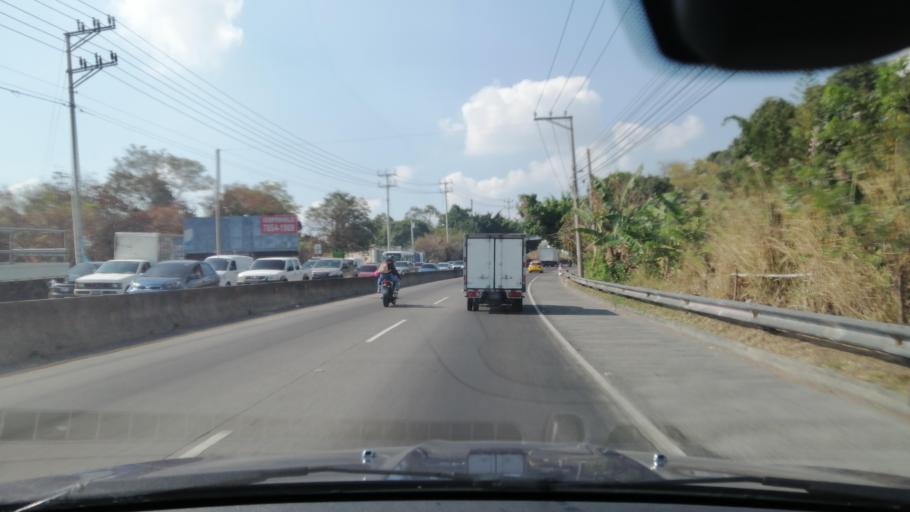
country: SV
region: San Salvador
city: Ayutuxtepeque
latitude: 13.7618
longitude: -89.2133
